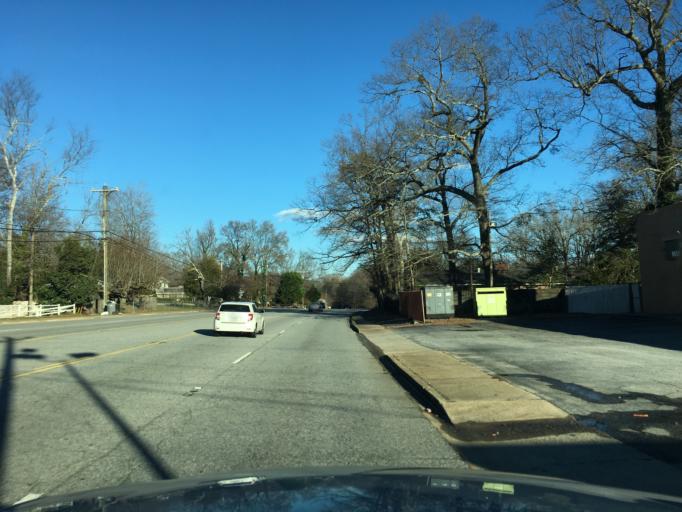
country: US
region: South Carolina
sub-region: Greenville County
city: Wade Hampton
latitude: 34.8711
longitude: -82.3427
